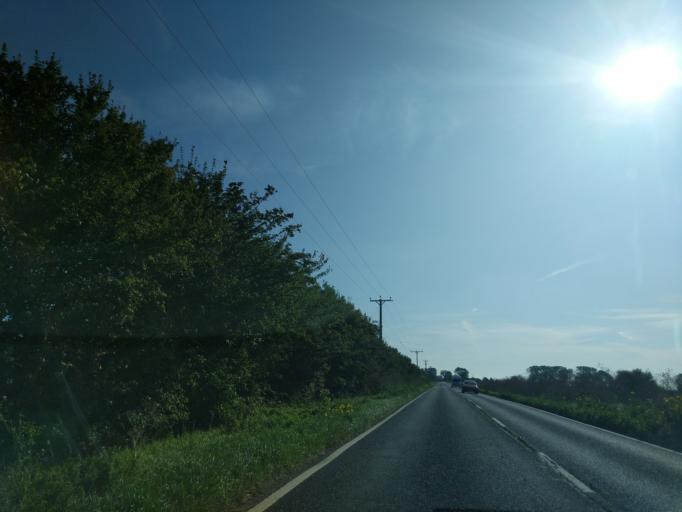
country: GB
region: England
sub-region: Lincolnshire
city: Bourne
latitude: 52.7721
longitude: -0.3022
